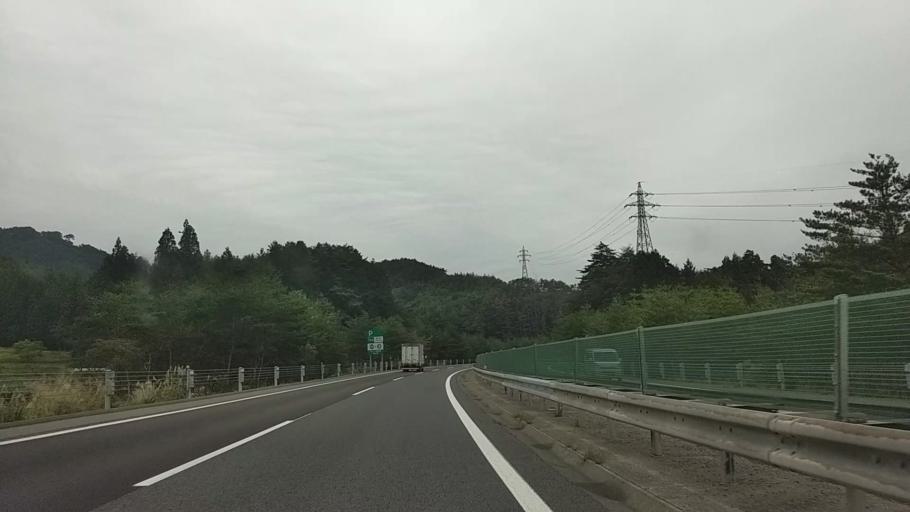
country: JP
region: Nagano
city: Omachi
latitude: 36.4411
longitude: 138.0387
